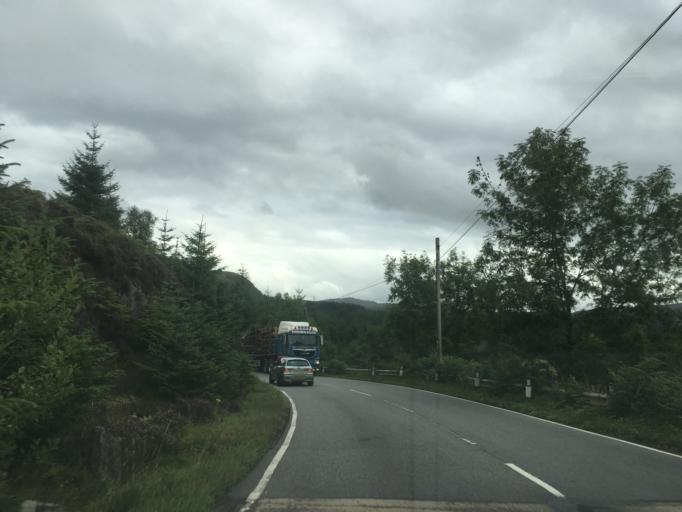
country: GB
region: Scotland
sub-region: Argyll and Bute
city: Oban
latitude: 56.2789
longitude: -5.4837
